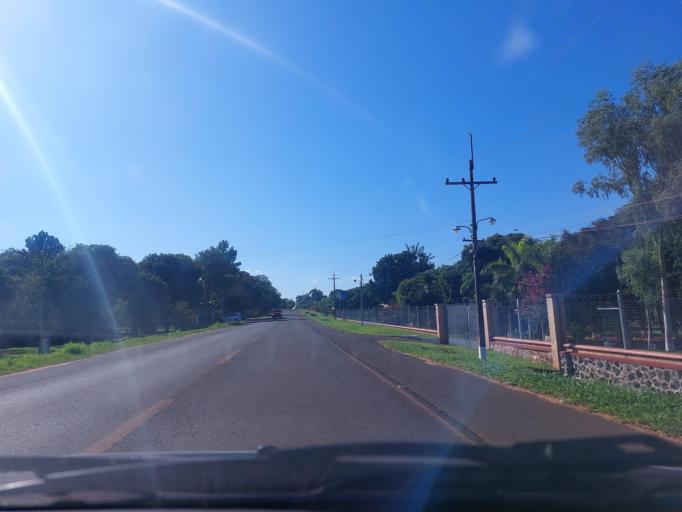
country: PY
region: San Pedro
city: Guayaybi
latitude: -24.5316
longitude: -56.4573
